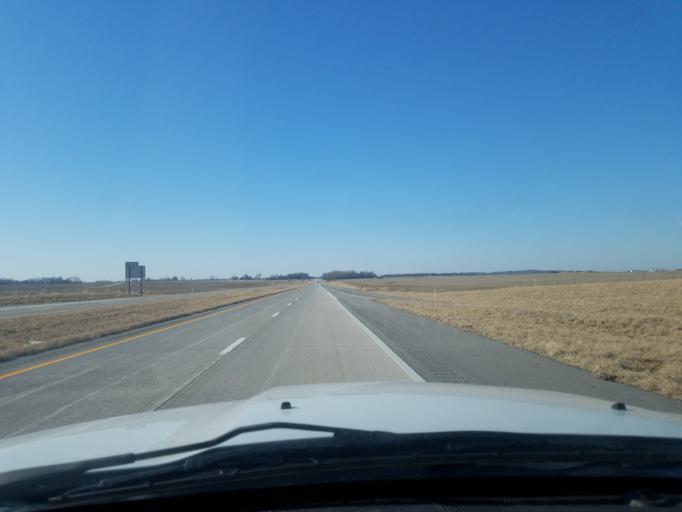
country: US
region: Kentucky
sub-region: Henderson County
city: Henderson
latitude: 37.7874
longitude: -87.4751
